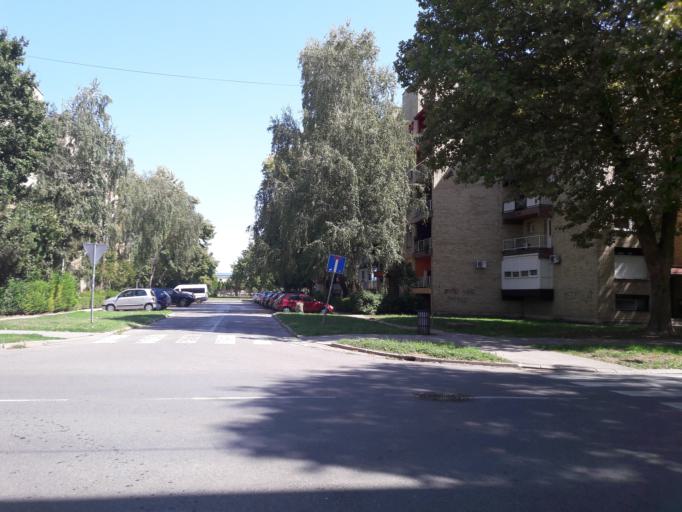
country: HR
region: Osjecko-Baranjska
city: Visnjevac
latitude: 45.5624
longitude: 18.6530
